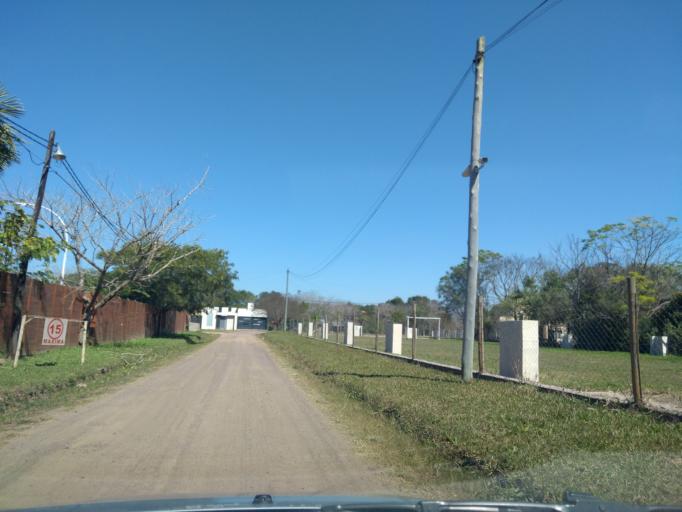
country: AR
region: Chaco
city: Resistencia
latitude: -27.4332
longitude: -58.9482
